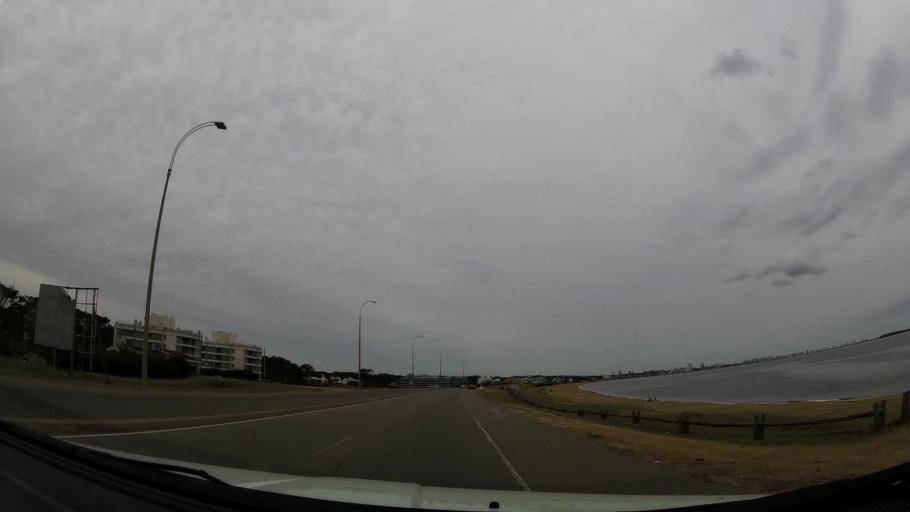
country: UY
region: Maldonado
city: Maldonado
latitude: -34.9091
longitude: -55.0118
